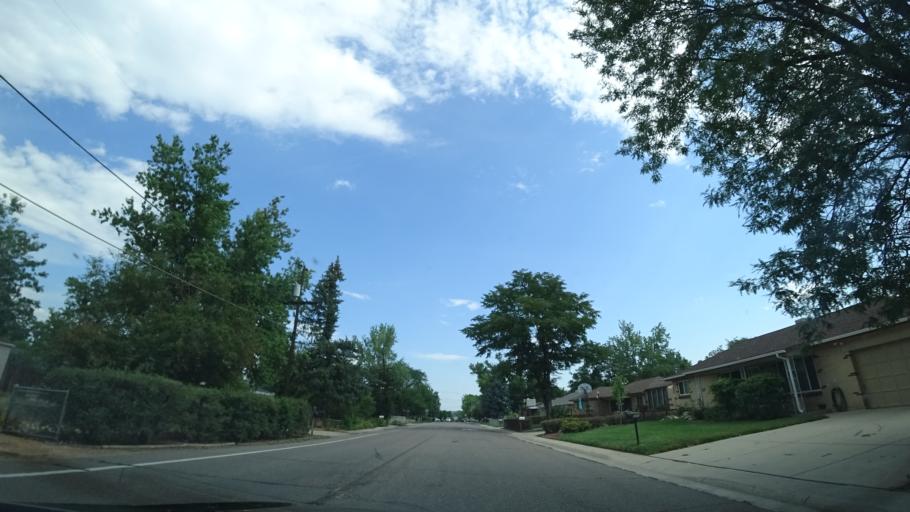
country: US
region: Colorado
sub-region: Jefferson County
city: Lakewood
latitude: 39.7222
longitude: -105.0627
